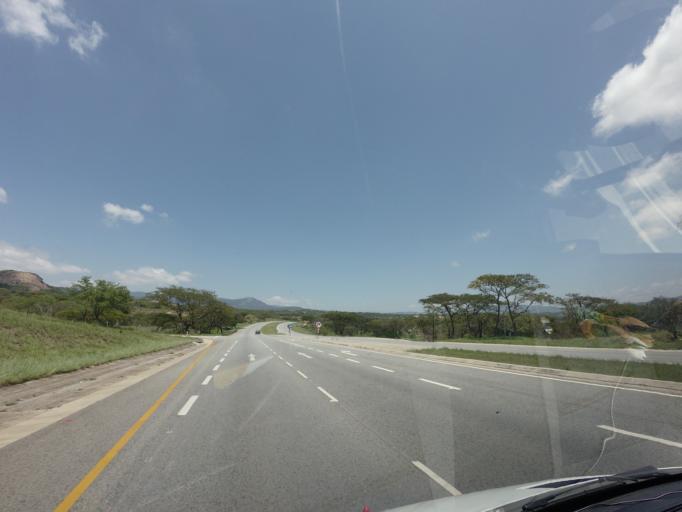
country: ZA
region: Mpumalanga
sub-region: Ehlanzeni District
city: Nelspruit
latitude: -25.4463
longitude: 30.8688
